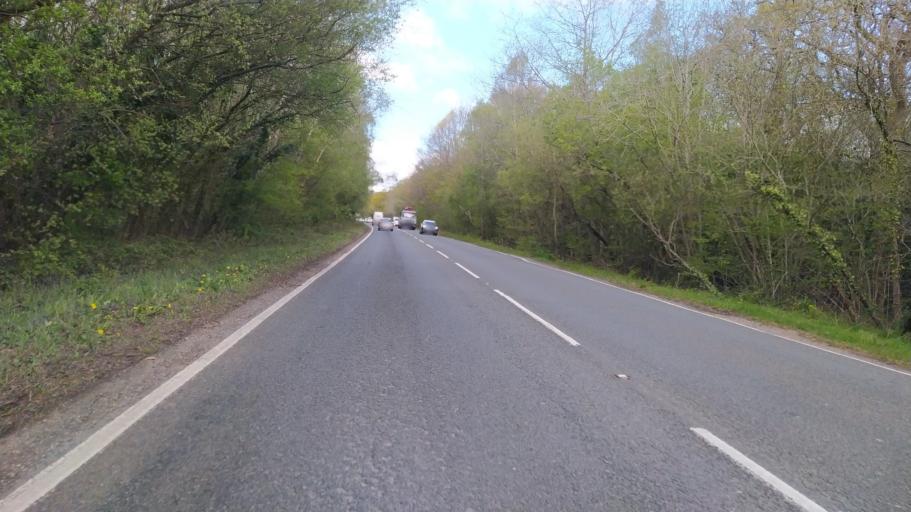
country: GB
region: England
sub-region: Hampshire
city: Marchwood
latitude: 50.8960
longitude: -1.4749
